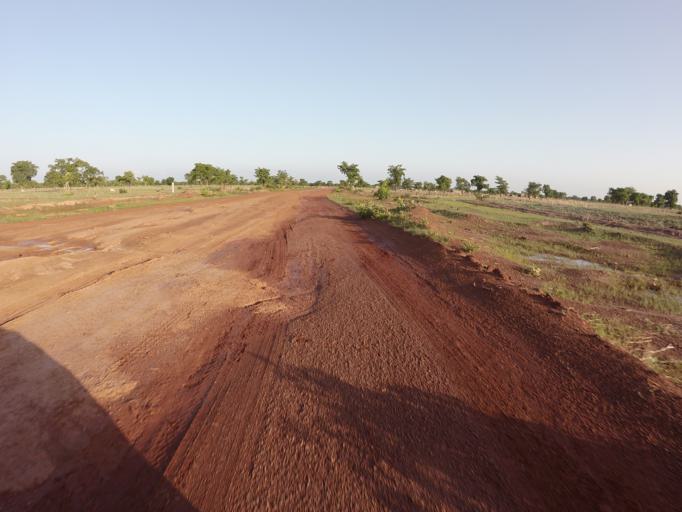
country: TG
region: Savanes
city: Sansanne-Mango
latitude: 10.2937
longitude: -0.0878
